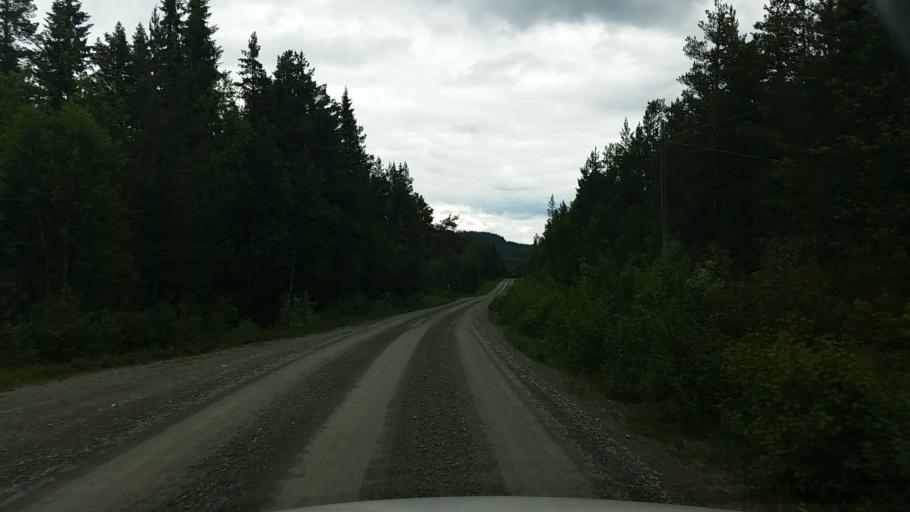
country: NO
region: Hedmark
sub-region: Engerdal
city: Engerdal
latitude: 62.4236
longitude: 12.6768
